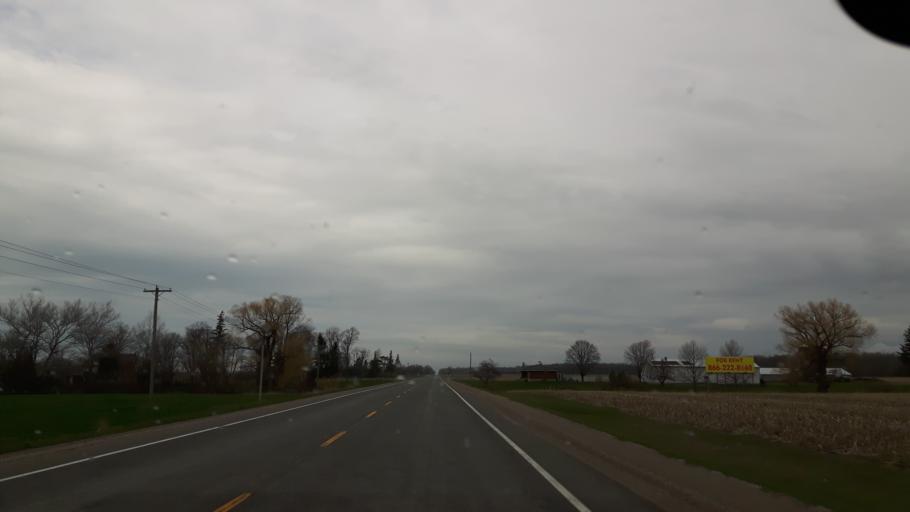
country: CA
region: Ontario
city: Goderich
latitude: 43.6304
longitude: -81.7056
